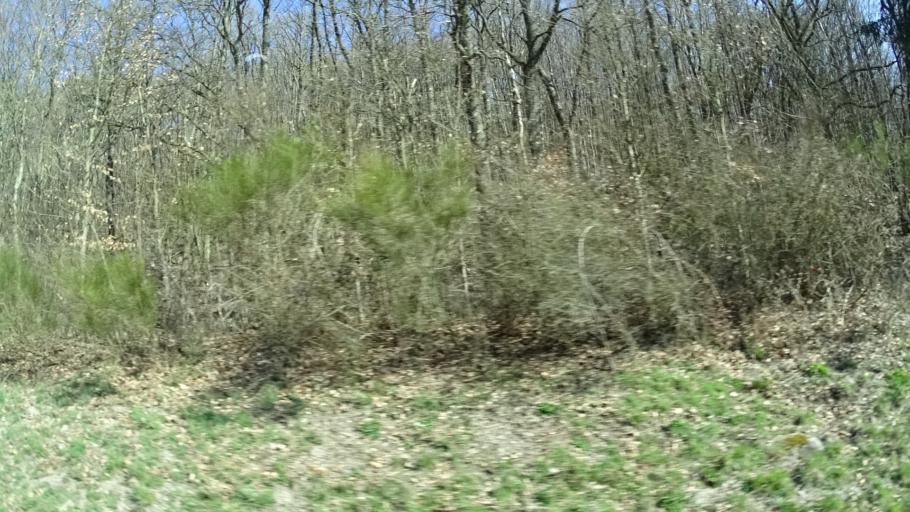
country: DE
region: Rheinland-Pfalz
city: Oberhambach
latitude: 49.6827
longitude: 7.1749
